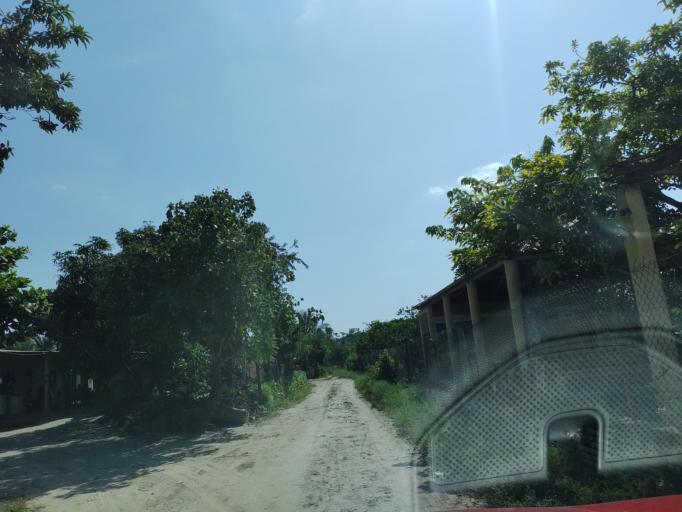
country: MX
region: Puebla
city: San Jose Acateno
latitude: 20.2564
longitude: -97.2078
